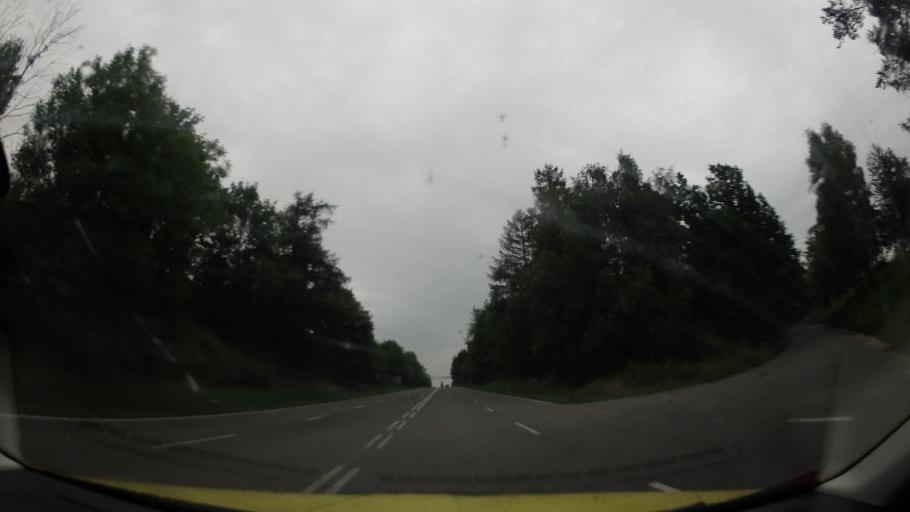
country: CZ
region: Olomoucky
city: Belotin
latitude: 49.5706
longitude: 17.7722
